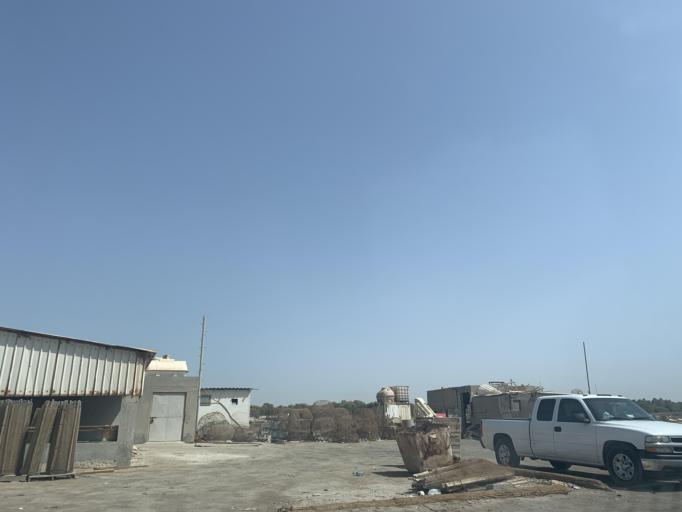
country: BH
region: Manama
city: Jidd Hafs
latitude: 26.2387
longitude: 50.5137
